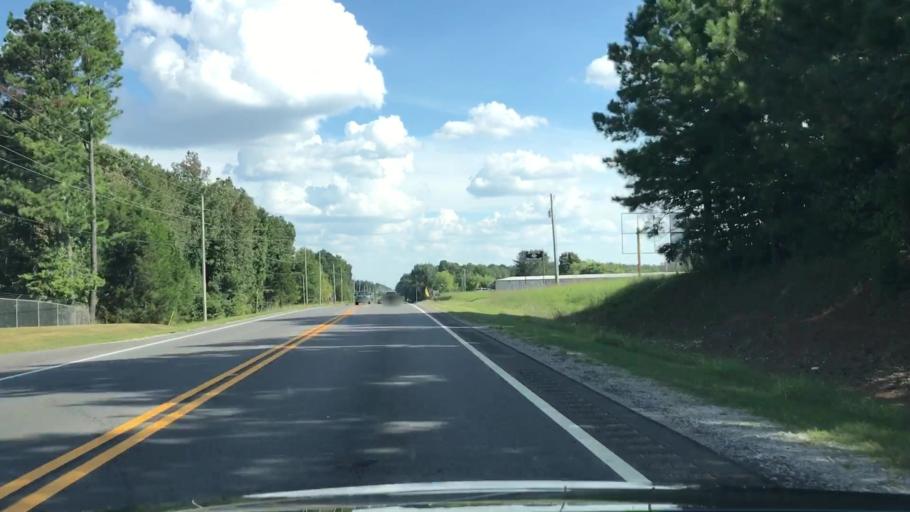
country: US
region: Alabama
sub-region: Madison County
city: Harvest
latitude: 34.9136
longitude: -86.7598
